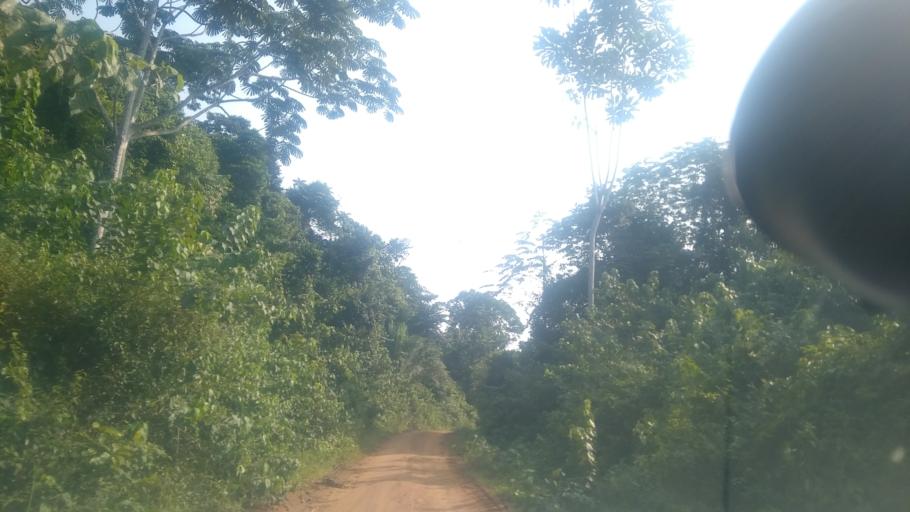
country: CM
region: South Province
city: Kribi
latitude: 2.6497
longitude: 9.8496
